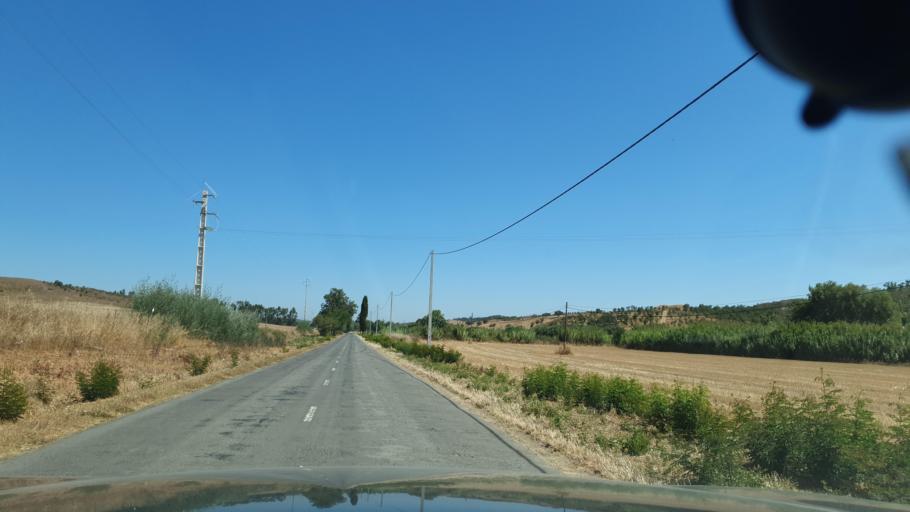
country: PT
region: Faro
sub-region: Monchique
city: Monchique
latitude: 37.4482
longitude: -8.4873
